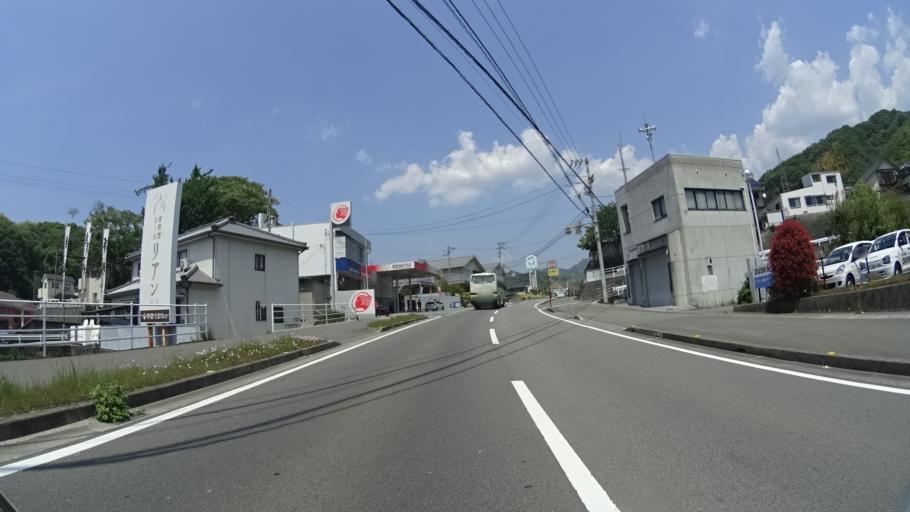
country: JP
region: Ehime
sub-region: Shikoku-chuo Shi
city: Matsuyama
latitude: 33.8553
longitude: 132.8103
